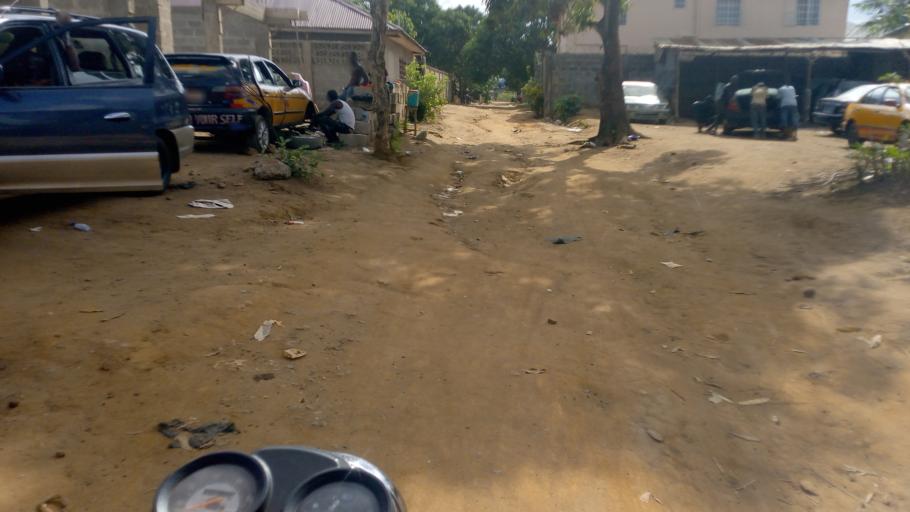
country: SL
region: Western Area
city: Waterloo
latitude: 8.3223
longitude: -13.0731
